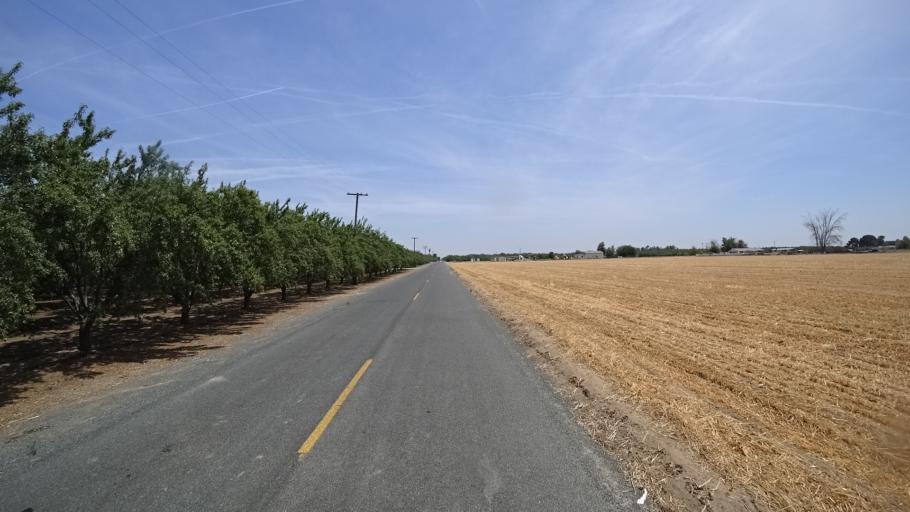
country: US
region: California
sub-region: Fresno County
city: Riverdale
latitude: 36.3947
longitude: -119.8728
